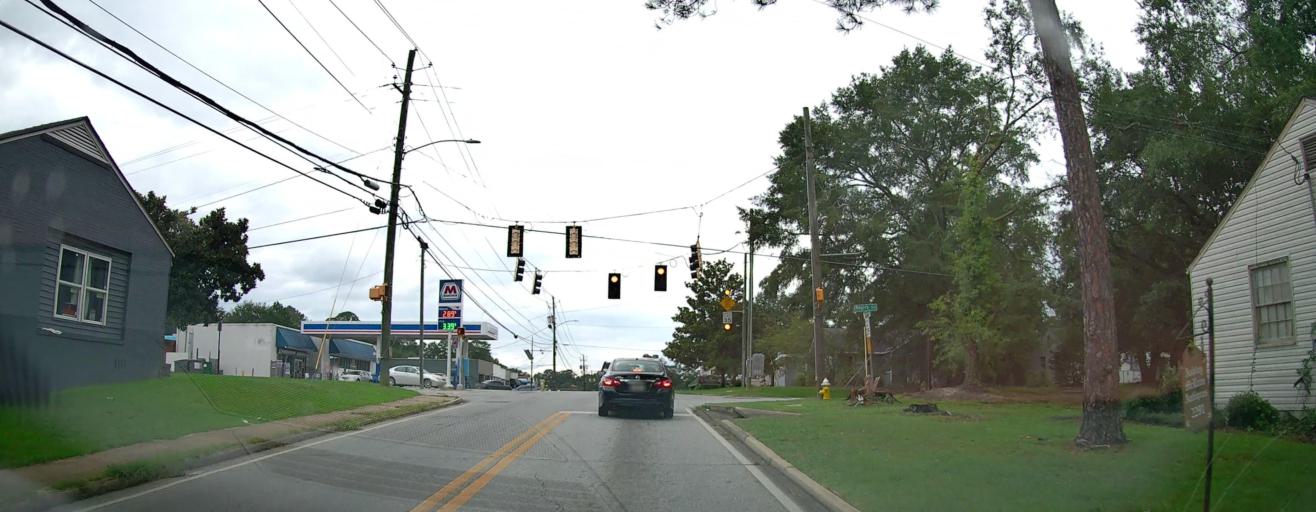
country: US
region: Georgia
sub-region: Bibb County
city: Macon
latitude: 32.8538
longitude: -83.6540
